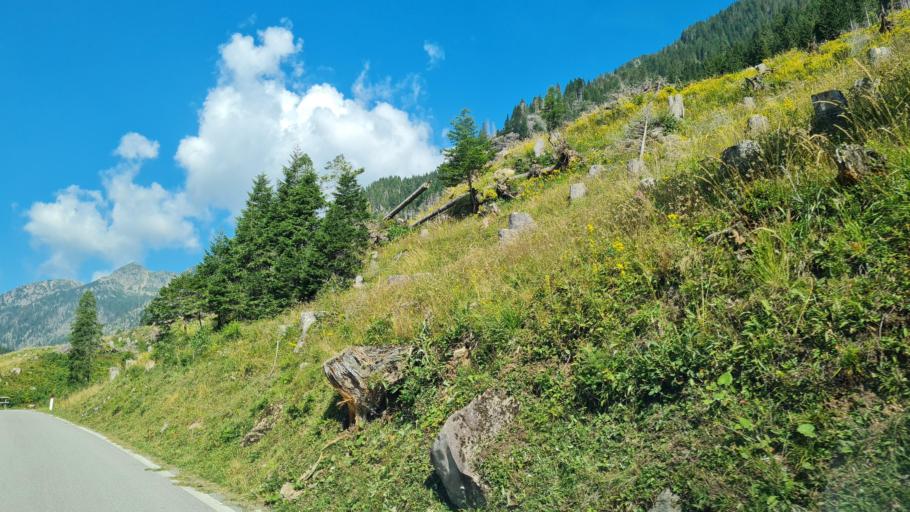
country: IT
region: Trentino-Alto Adige
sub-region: Provincia di Trento
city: Torcegno
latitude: 46.1494
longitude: 11.4544
